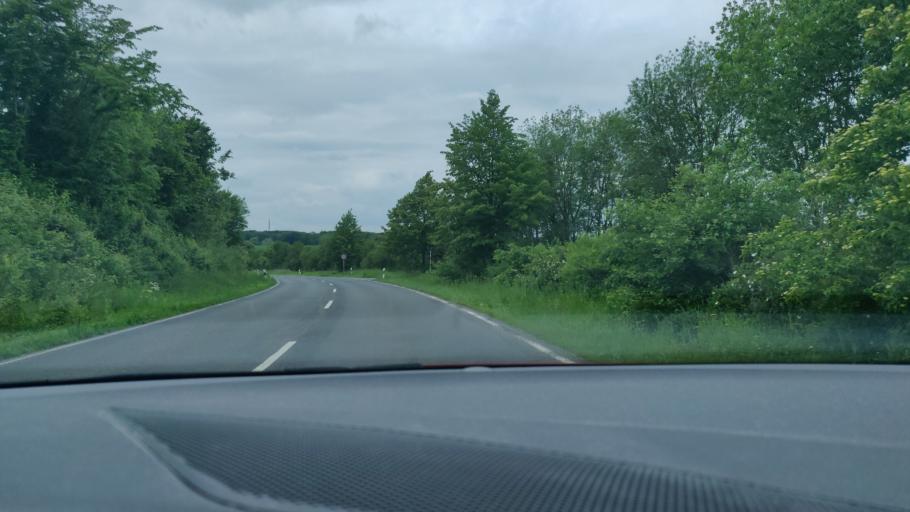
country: DE
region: North Rhine-Westphalia
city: Wulfrath
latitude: 51.2971
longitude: 7.0799
